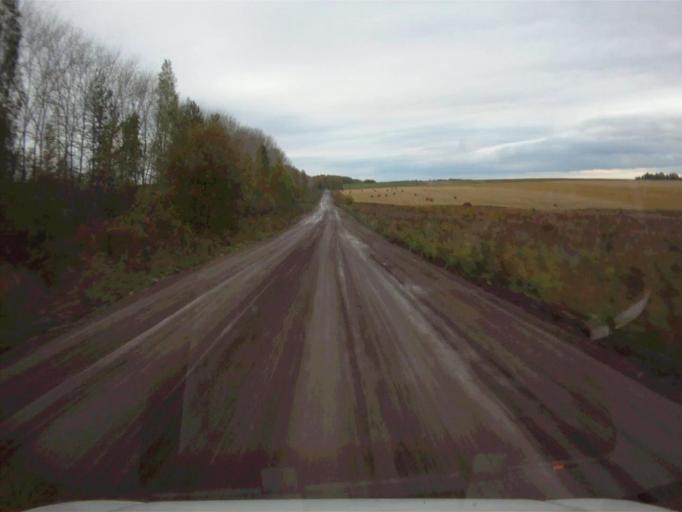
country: RU
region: Sverdlovsk
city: Mikhaylovsk
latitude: 56.1630
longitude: 59.2422
